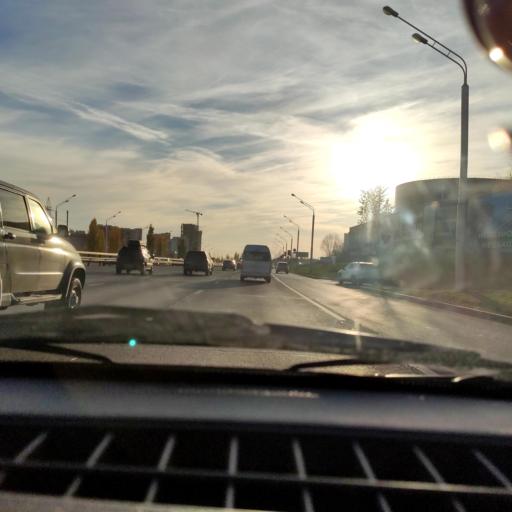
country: RU
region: Bashkortostan
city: Ufa
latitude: 54.7242
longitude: 55.9848
